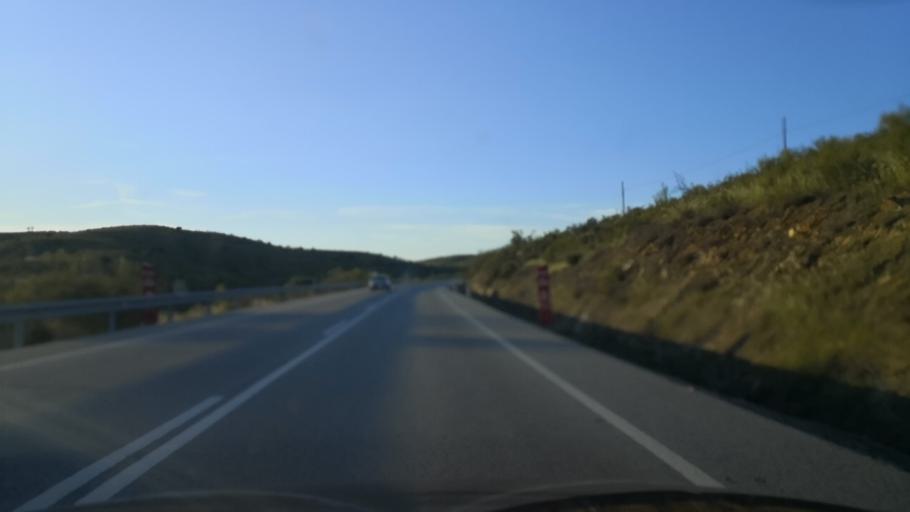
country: ES
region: Extremadura
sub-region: Provincia de Caceres
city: Valencia de Alcantara
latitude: 39.4752
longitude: -7.2118
